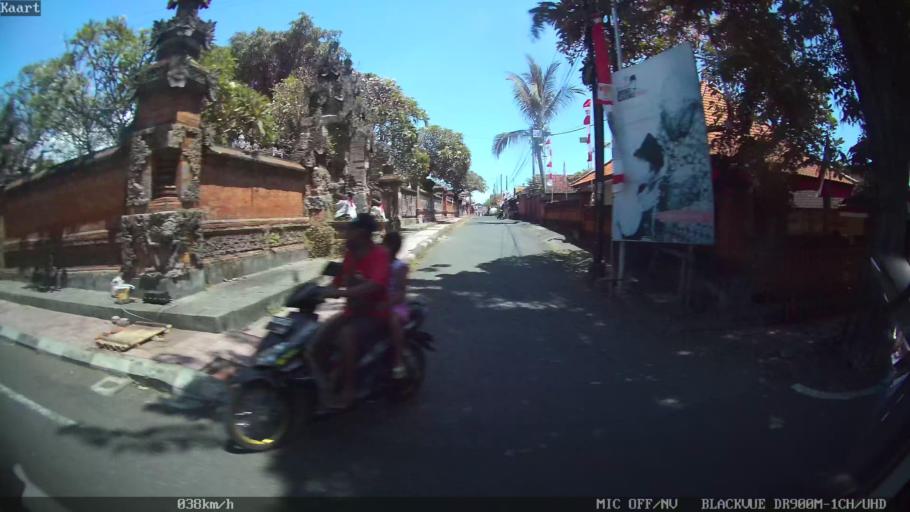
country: ID
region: Bali
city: Banjar Liligundi
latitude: -8.1270
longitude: 115.0977
